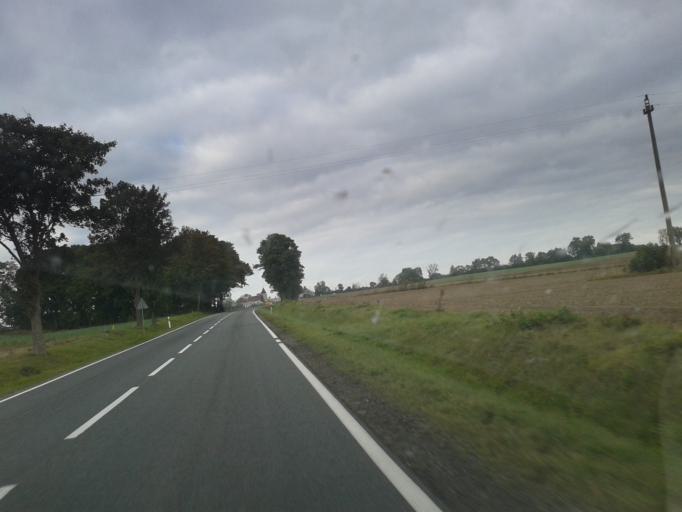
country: PL
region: Kujawsko-Pomorskie
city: Kamien Krajenski
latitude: 53.4957
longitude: 17.5098
